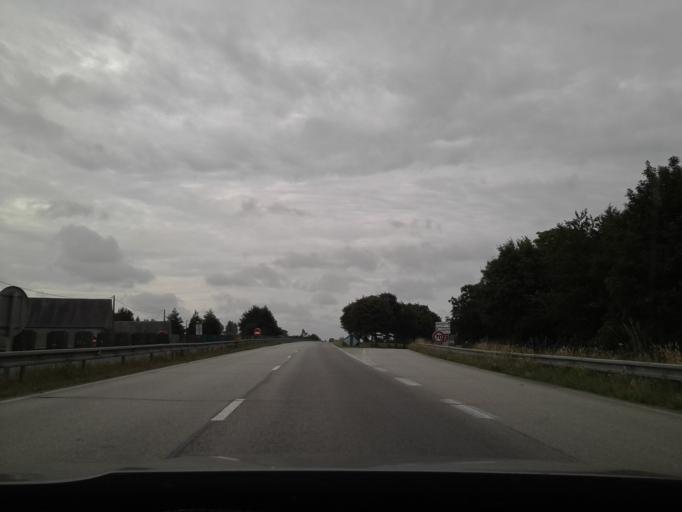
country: FR
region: Lower Normandy
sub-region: Departement de la Manche
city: Sainte-Mere-Eglise
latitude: 49.3825
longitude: -1.2977
